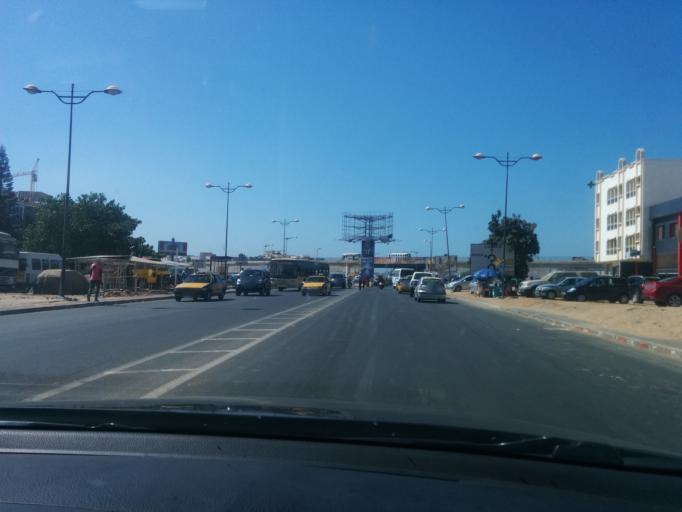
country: SN
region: Dakar
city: Mermoz Boabab
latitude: 14.7161
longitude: -17.4701
